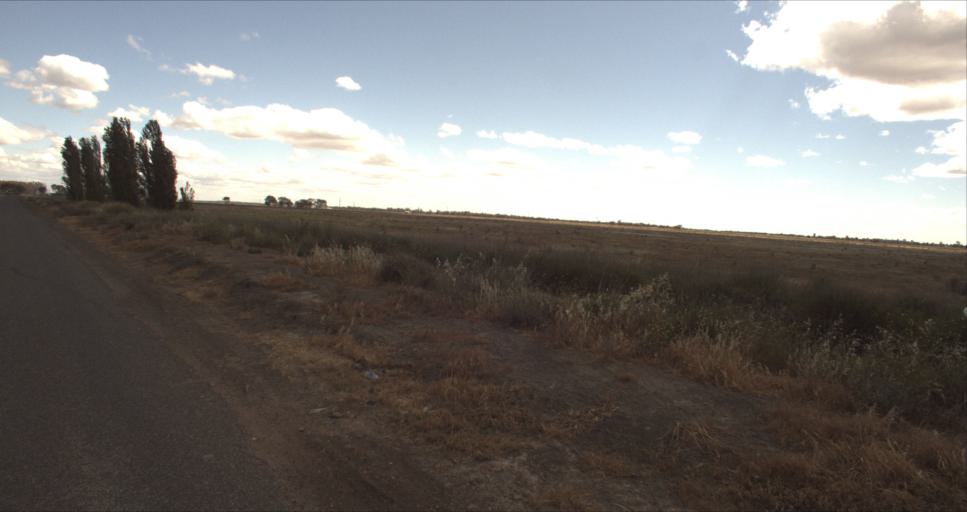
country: AU
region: New South Wales
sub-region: Leeton
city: Leeton
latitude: -34.5265
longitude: 146.2208
